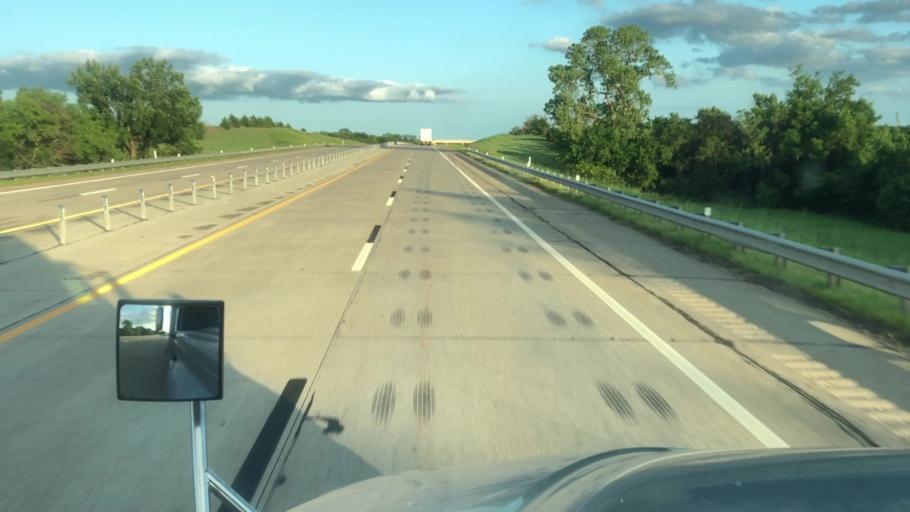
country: US
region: Oklahoma
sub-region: Pawnee County
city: Pawnee
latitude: 36.3237
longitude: -97.0024
